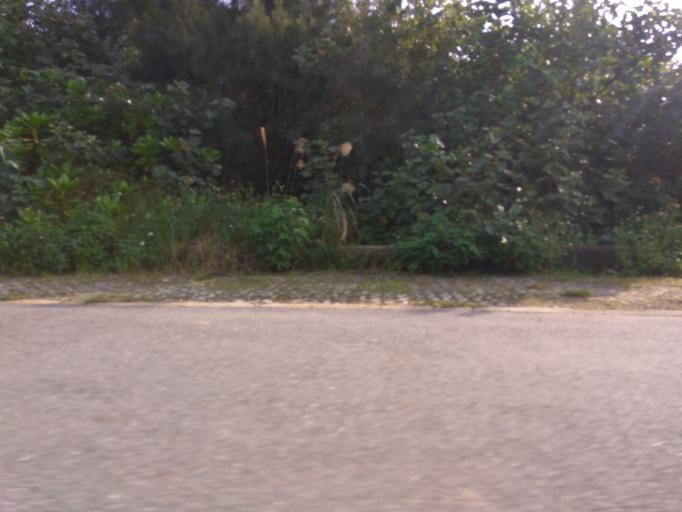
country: TW
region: Taiwan
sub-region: Hsinchu
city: Zhubei
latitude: 24.9864
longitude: 121.0167
